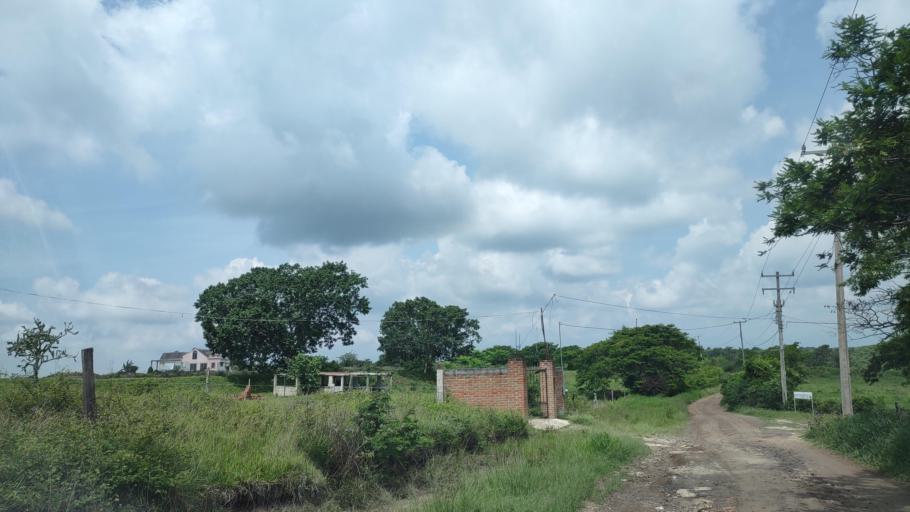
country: MX
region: Veracruz
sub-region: Emiliano Zapata
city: Dos Rios
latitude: 19.4631
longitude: -96.7951
